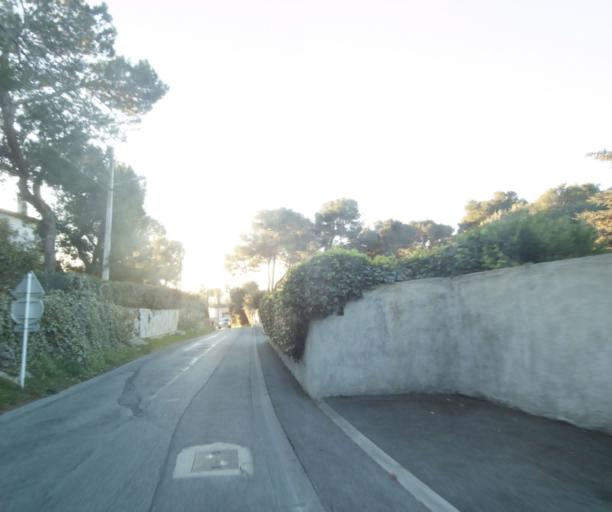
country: FR
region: Provence-Alpes-Cote d'Azur
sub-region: Departement des Alpes-Maritimes
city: Vallauris
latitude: 43.5816
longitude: 7.0817
